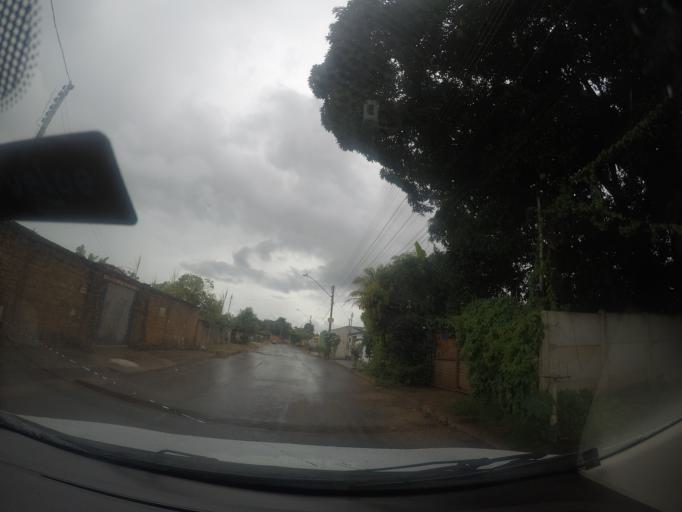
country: BR
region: Goias
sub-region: Trindade
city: Trindade
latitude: -16.6446
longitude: -49.3957
